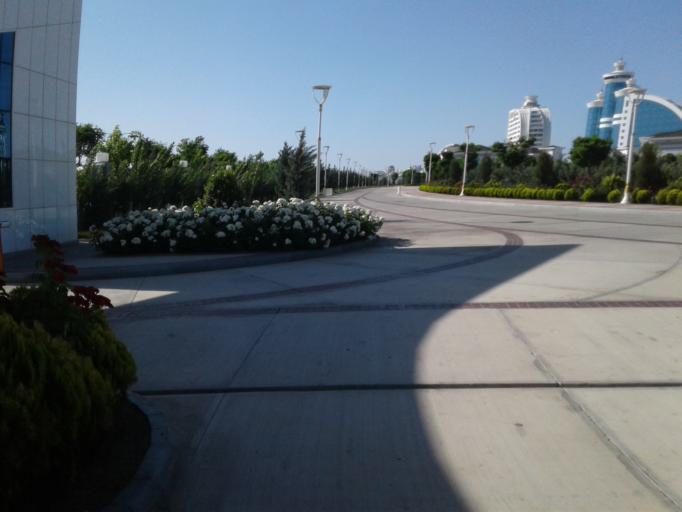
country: TM
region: Balkan
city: Turkmenbasy
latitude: 39.9848
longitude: 52.8247
